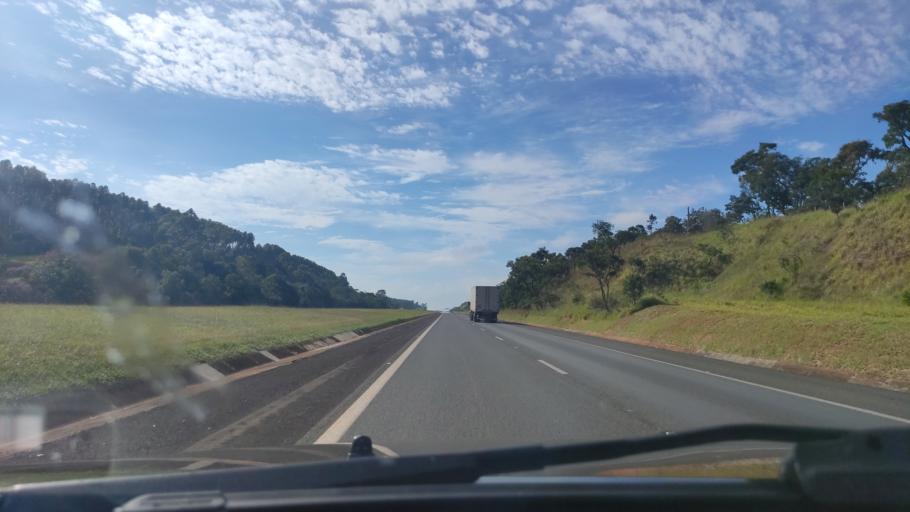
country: BR
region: Sao Paulo
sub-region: Itatinga
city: Itatinga
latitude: -23.0654
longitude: -48.5574
